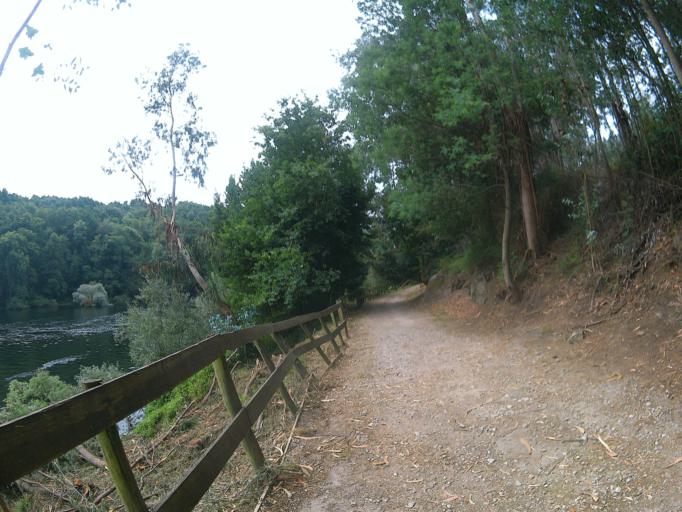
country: PT
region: Viana do Castelo
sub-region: Ponte de Lima
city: Ponte de Lima
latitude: 41.7756
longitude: -8.5565
